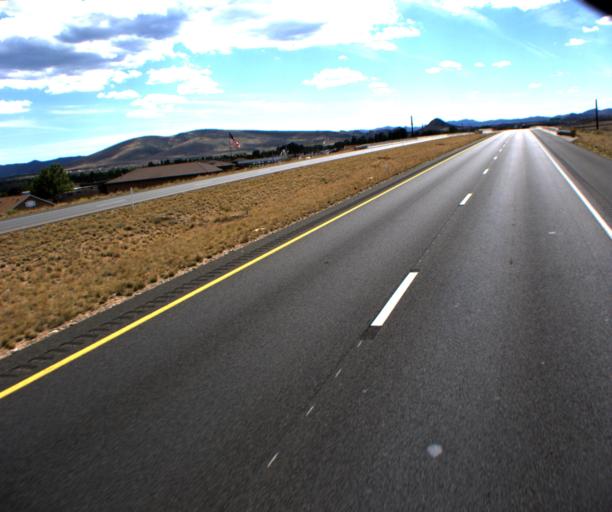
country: US
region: Arizona
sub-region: Yavapai County
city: Prescott Valley
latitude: 34.6375
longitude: -112.3313
